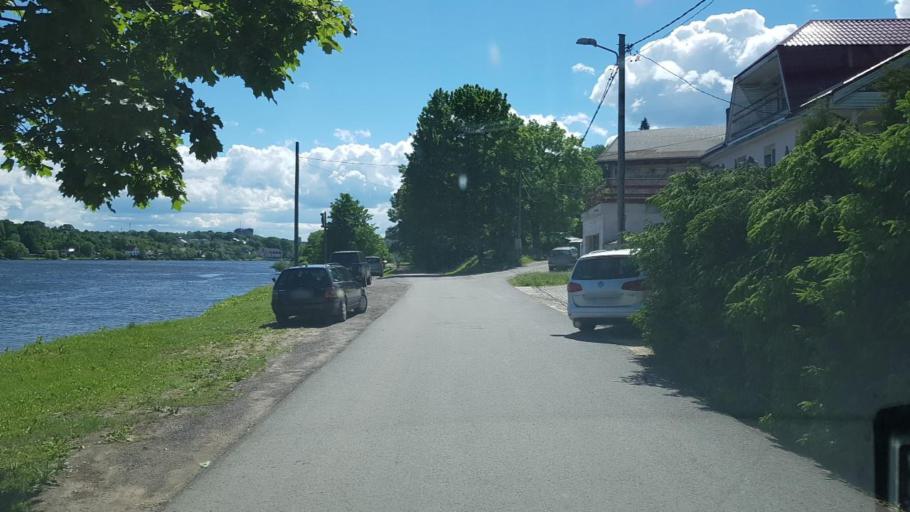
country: EE
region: Ida-Virumaa
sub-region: Narva linn
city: Narva
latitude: 59.3868
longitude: 28.2027
